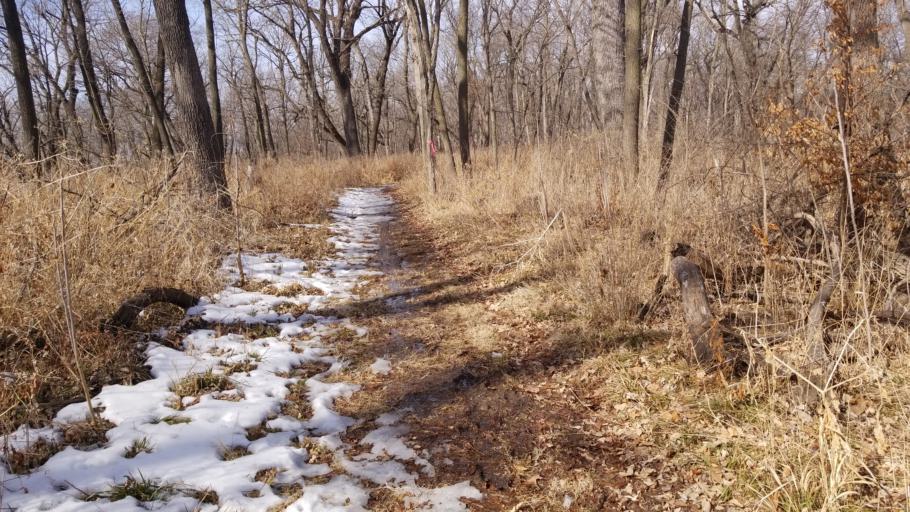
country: US
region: Nebraska
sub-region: Sarpy County
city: Bellevue
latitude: 41.1739
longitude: -95.9015
